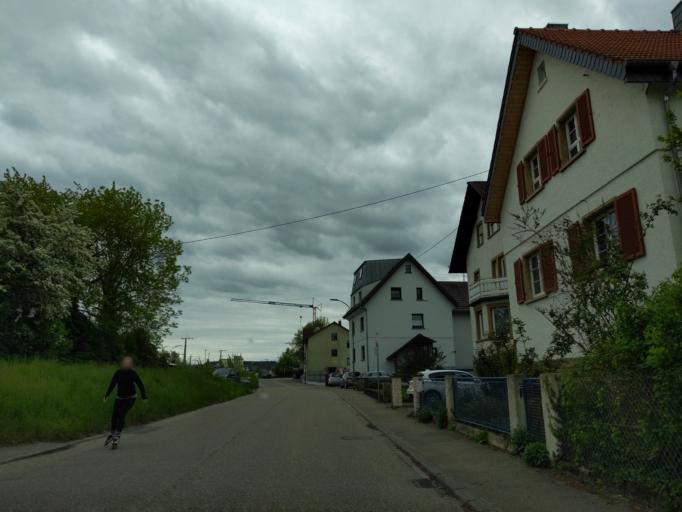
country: DE
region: Baden-Wuerttemberg
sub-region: Karlsruhe Region
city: Meckesheim
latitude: 49.3218
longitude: 8.8112
